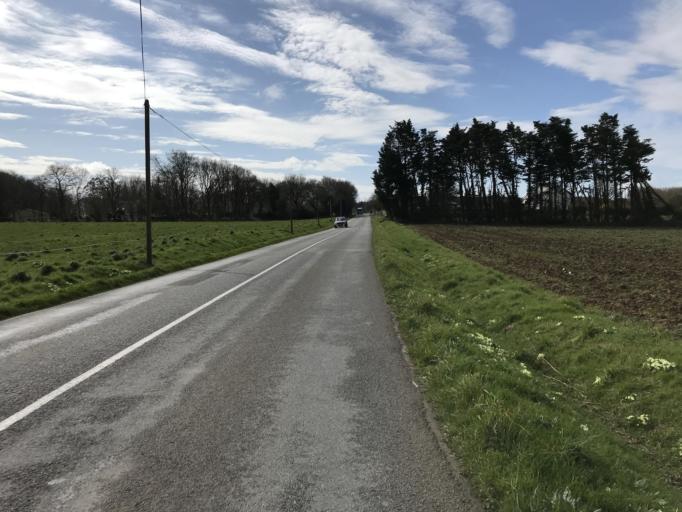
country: FR
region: Brittany
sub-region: Departement du Finistere
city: Dirinon
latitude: 48.3850
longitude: -4.2663
